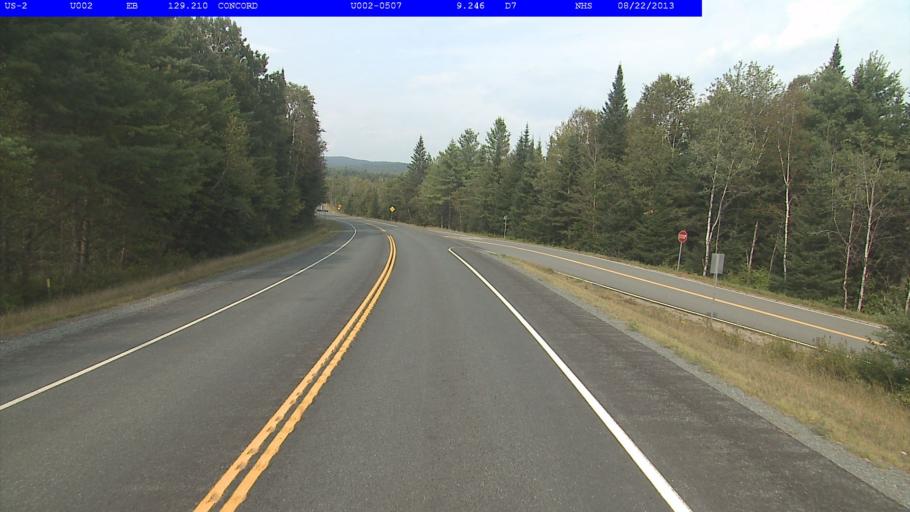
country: US
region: New Hampshire
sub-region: Grafton County
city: Littleton
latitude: 44.4509
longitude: -71.7923
